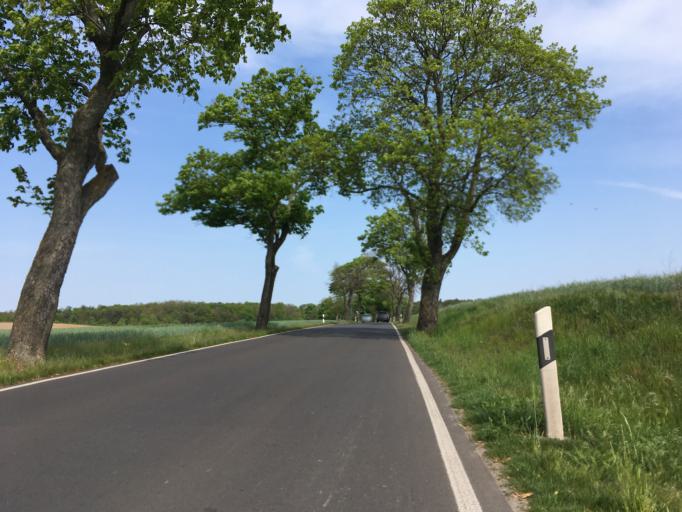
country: DE
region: Brandenburg
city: Werneuchen
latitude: 52.6081
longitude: 13.7577
